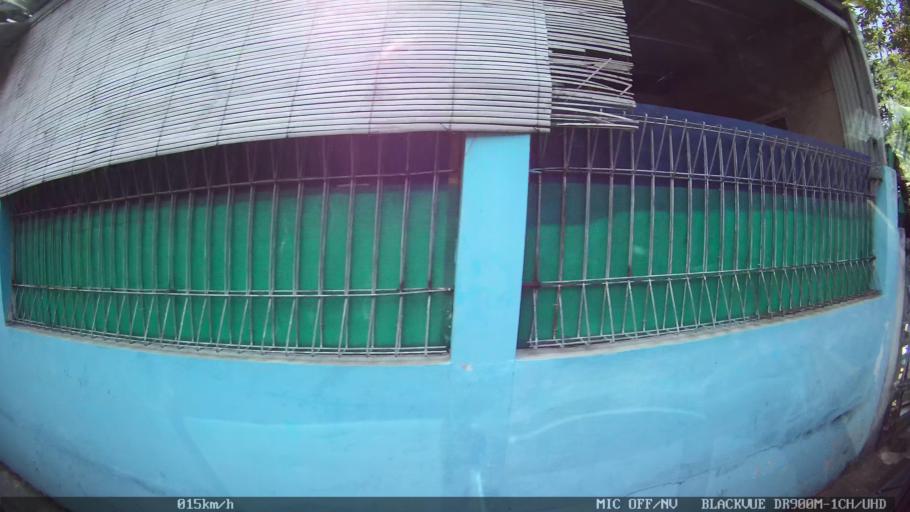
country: ID
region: Daerah Istimewa Yogyakarta
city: Yogyakarta
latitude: -7.8054
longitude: 110.4002
